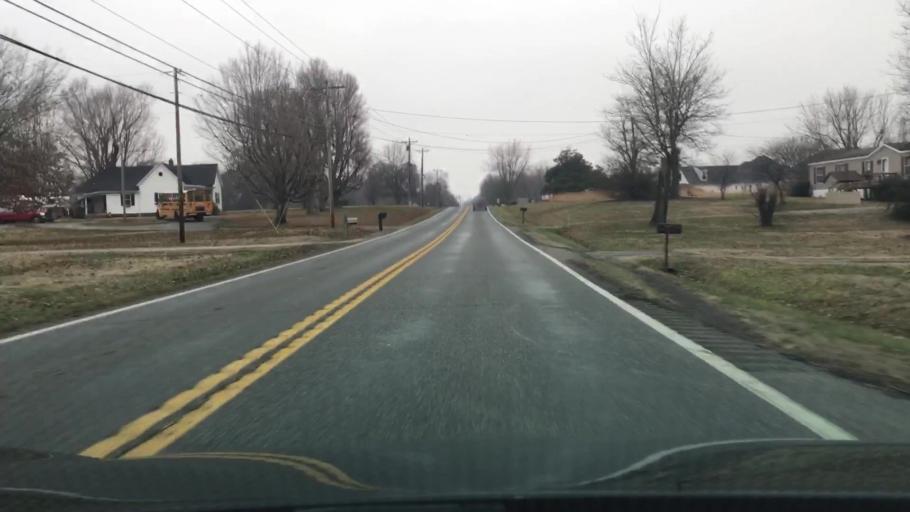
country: US
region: Kentucky
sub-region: Livingston County
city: Ledbetter
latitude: 36.9704
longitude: -88.4619
